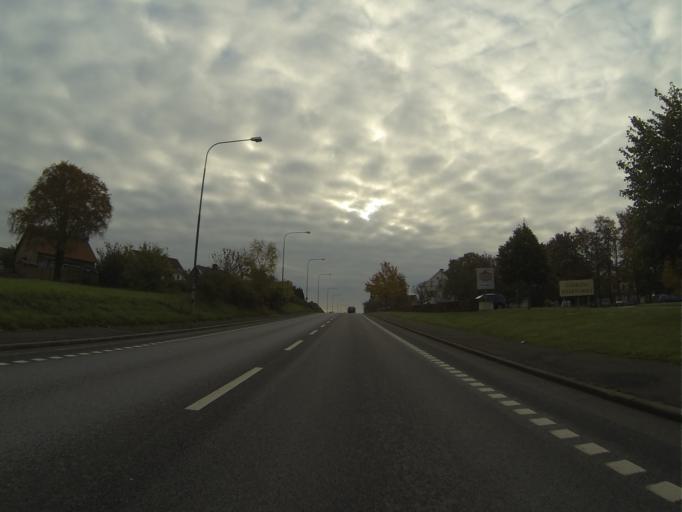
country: SE
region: Skane
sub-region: Tomelilla Kommun
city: Tomelilla
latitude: 55.5513
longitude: 13.9400
